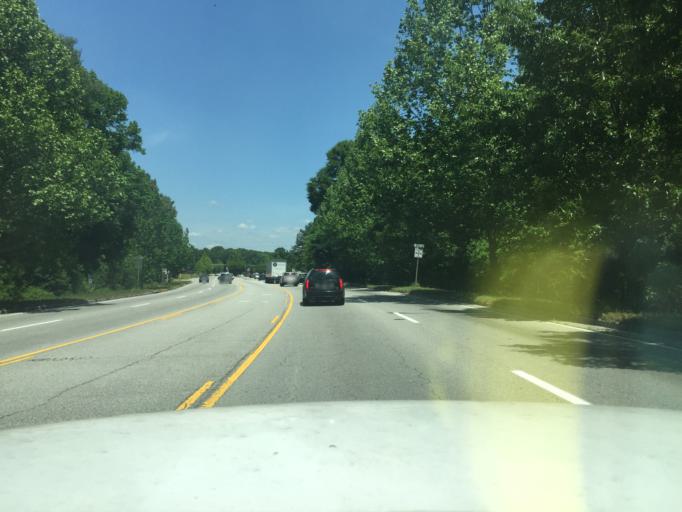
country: US
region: Georgia
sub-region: Chatham County
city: Garden City
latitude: 32.0597
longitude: -81.1610
